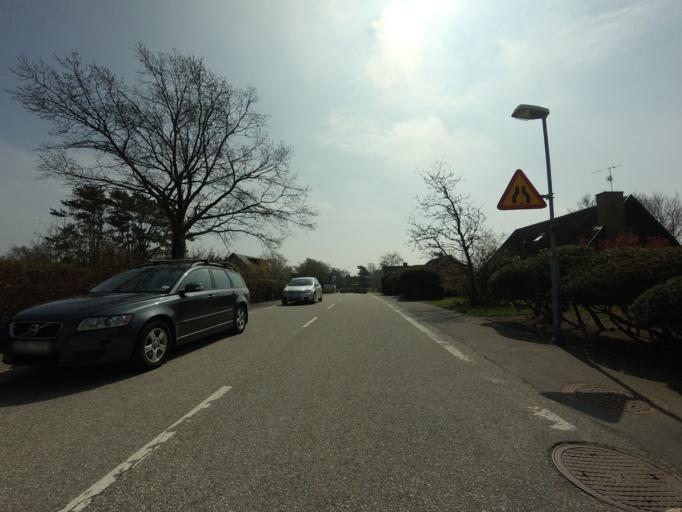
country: SE
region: Skane
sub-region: Skurups Kommun
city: Skivarp
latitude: 55.3928
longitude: 13.5951
